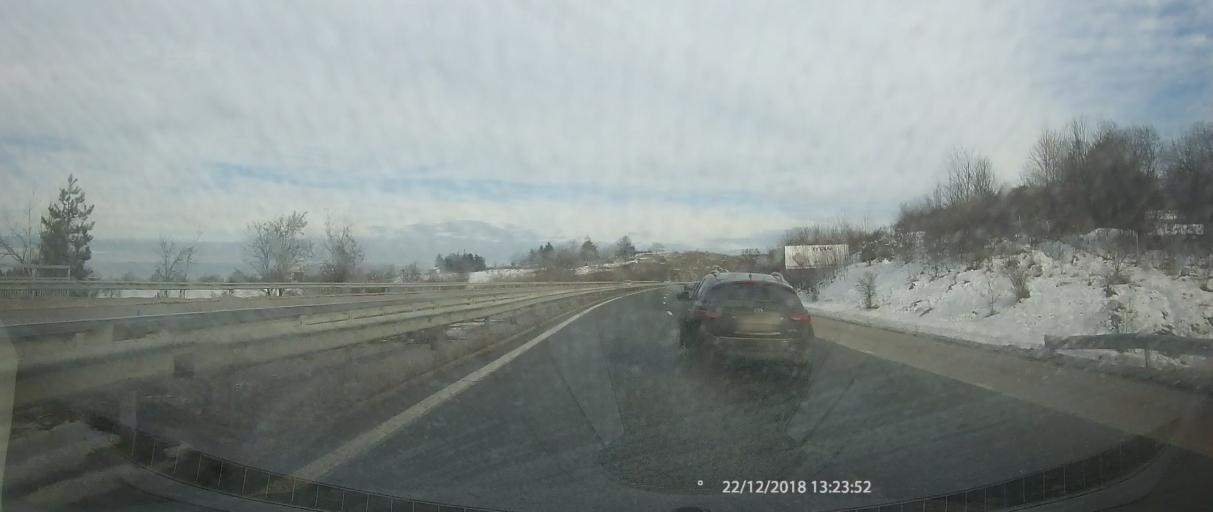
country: BG
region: Lovech
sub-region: Obshtina Yablanitsa
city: Yablanitsa
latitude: 43.0109
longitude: 24.0945
